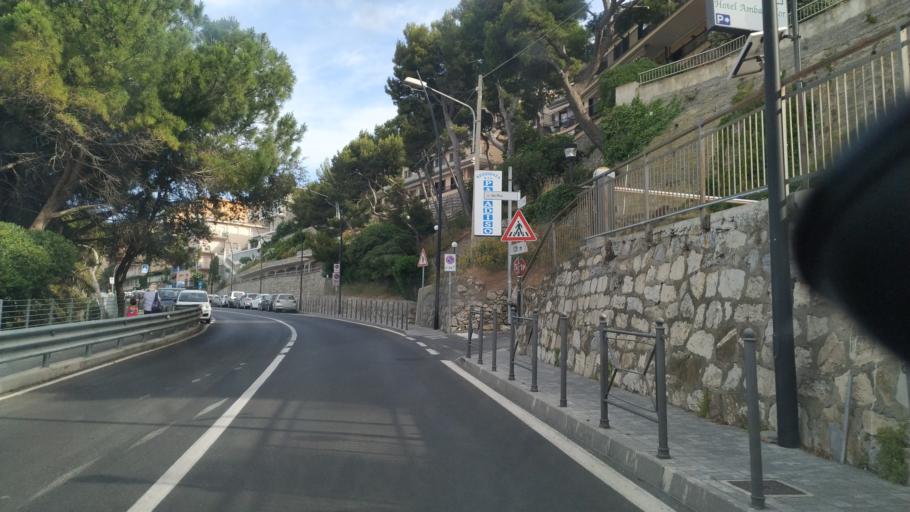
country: IT
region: Liguria
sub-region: Provincia di Savona
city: Laigueglia
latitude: 43.9698
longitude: 8.1611
